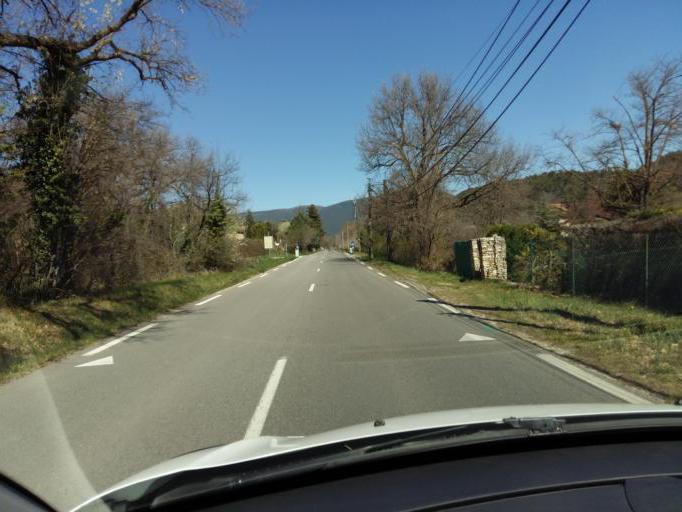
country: FR
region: Provence-Alpes-Cote d'Azur
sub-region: Departement du Vaucluse
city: Saignon
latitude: 43.8864
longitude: 5.4255
